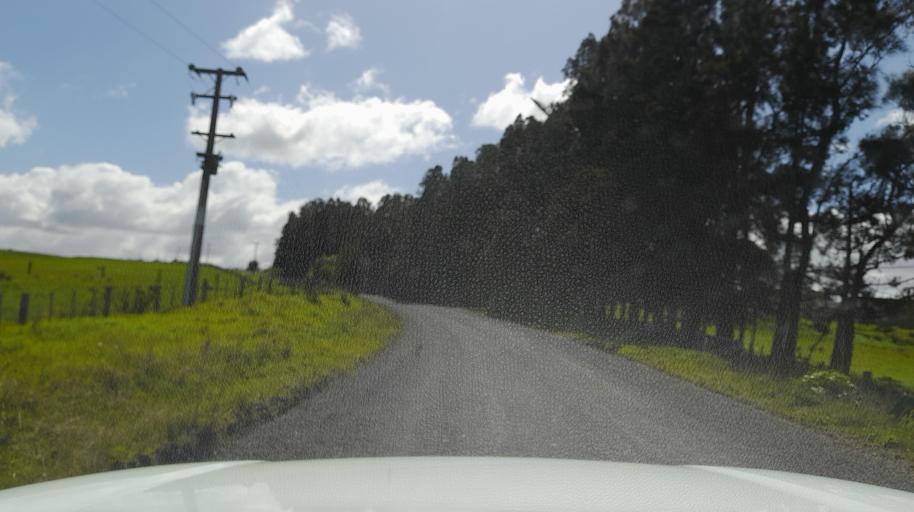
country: NZ
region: Northland
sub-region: Far North District
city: Kerikeri
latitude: -35.2260
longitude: 173.8756
